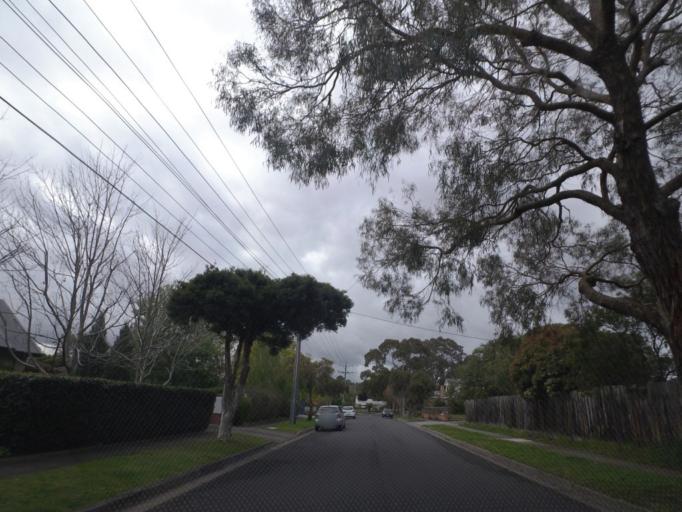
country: AU
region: Victoria
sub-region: Whitehorse
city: Blackburn North
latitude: -37.8145
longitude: 145.1430
